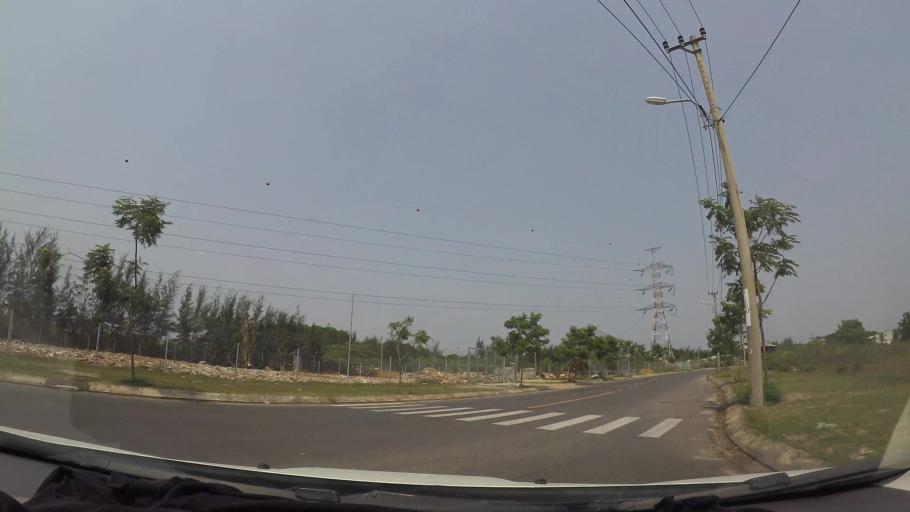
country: VN
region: Da Nang
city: Cam Le
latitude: 15.9937
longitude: 108.2046
